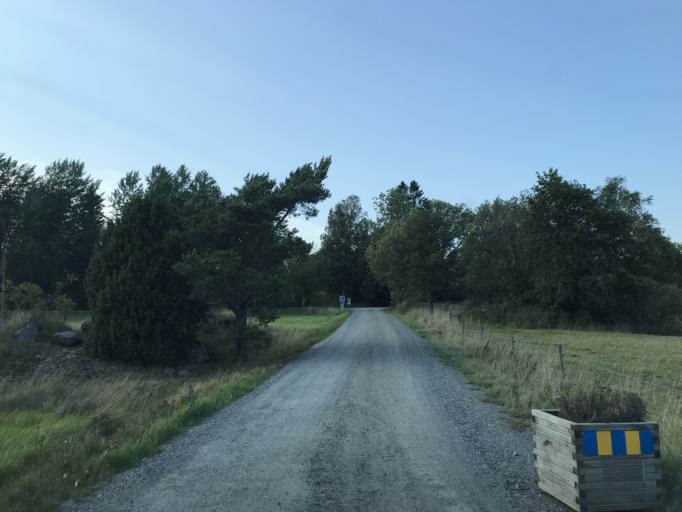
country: SE
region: Stockholm
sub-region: Norrtalje Kommun
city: Bjorko
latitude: 59.8502
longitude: 19.0130
